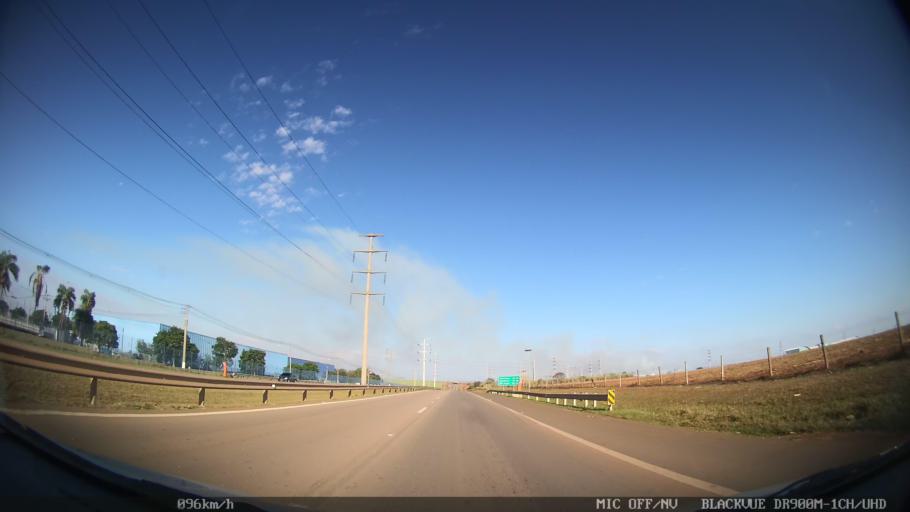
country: BR
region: Sao Paulo
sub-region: Piracicaba
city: Piracicaba
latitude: -22.6698
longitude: -47.6034
